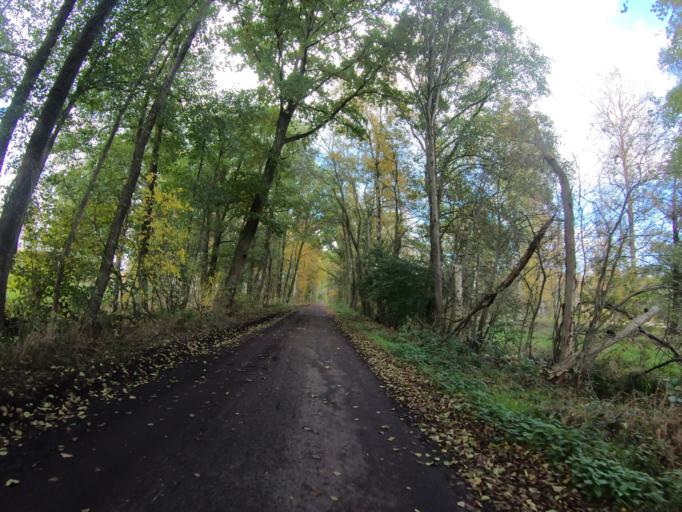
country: DE
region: Lower Saxony
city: Wagenhoff
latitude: 52.5457
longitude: 10.5615
